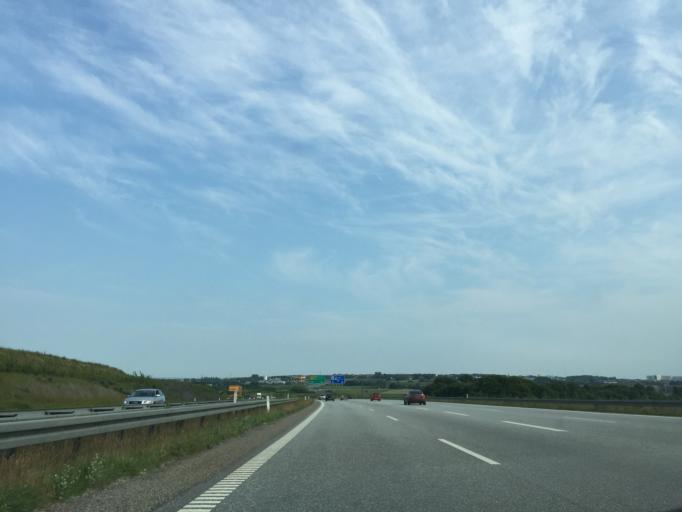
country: DK
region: Central Jutland
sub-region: Arhus Kommune
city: Trige
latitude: 56.2135
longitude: 10.1461
